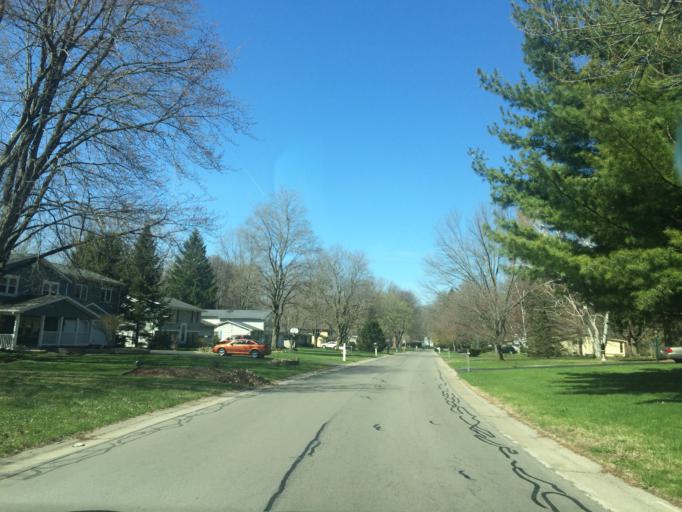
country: US
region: New York
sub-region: Monroe County
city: Fairport
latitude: 43.0940
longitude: -77.4643
